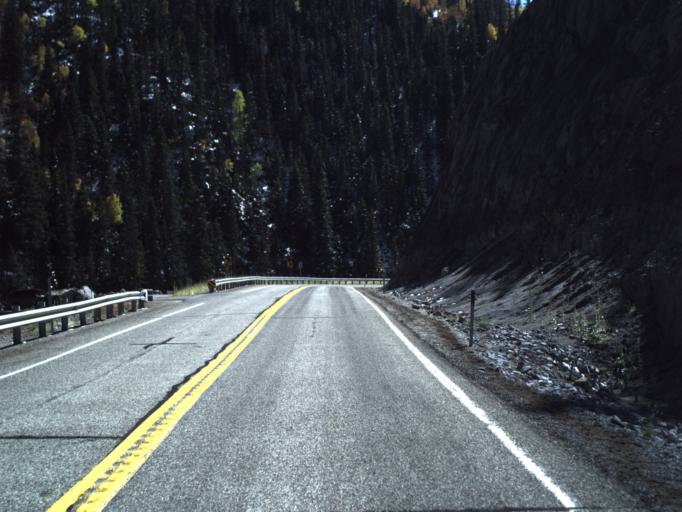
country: US
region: Utah
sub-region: Beaver County
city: Beaver
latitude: 38.2873
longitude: -112.4446
